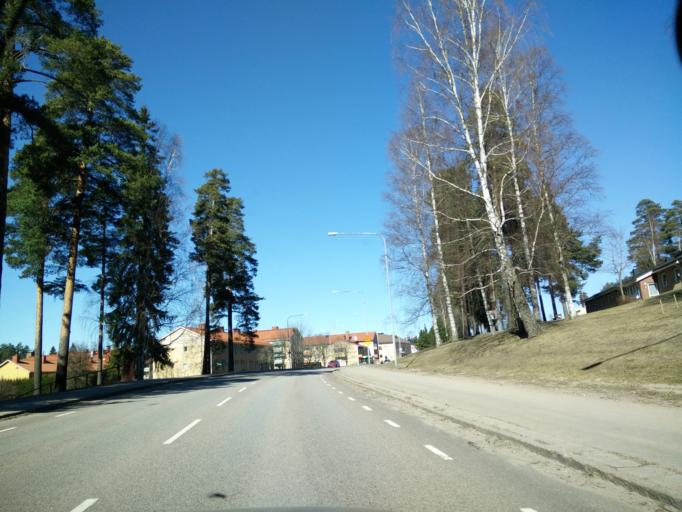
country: SE
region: Vaermland
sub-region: Hagfors Kommun
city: Hagfors
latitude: 60.0289
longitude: 13.6994
